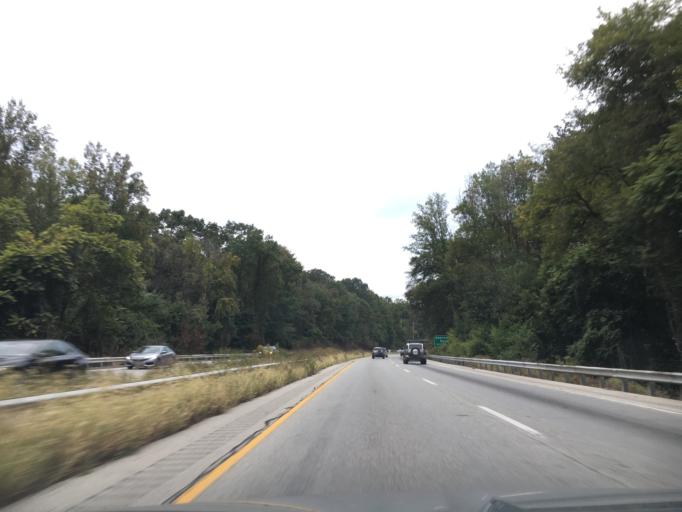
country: US
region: Pennsylvania
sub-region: Chester County
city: Caln
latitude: 40.0047
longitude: -75.7742
